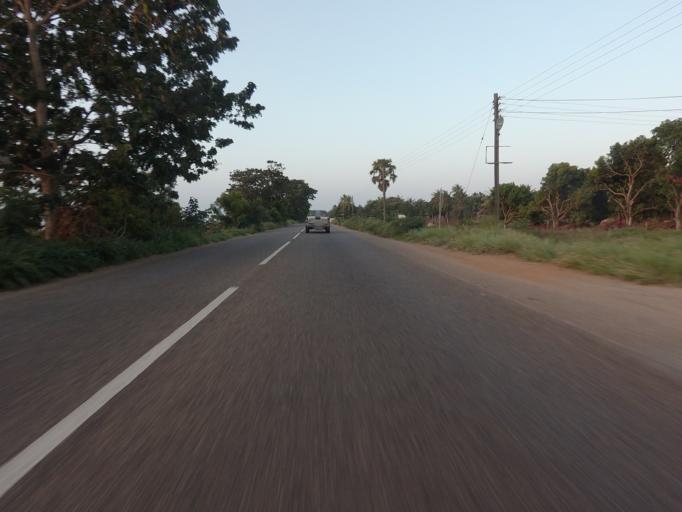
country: GH
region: Volta
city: Anloga
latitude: 5.8135
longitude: 0.9371
